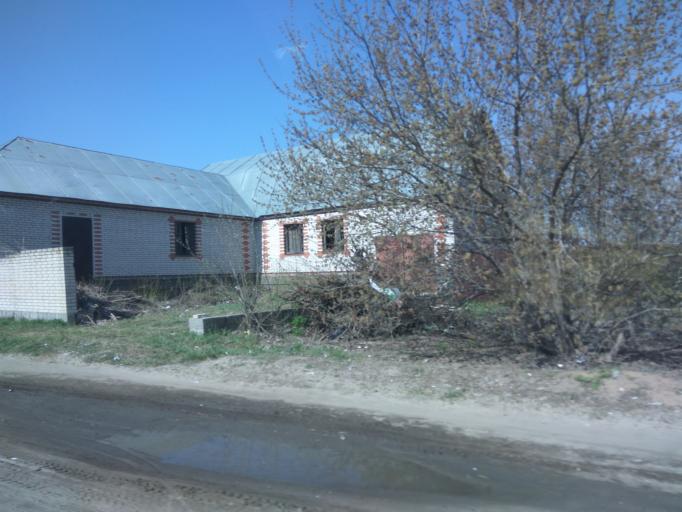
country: RU
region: Moskovskaya
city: Ramenskoye
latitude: 55.5479
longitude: 38.2506
